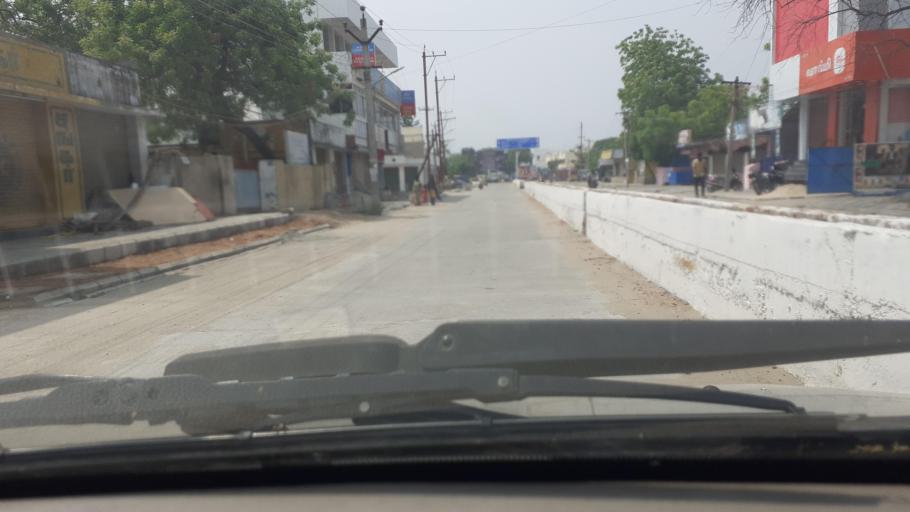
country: IN
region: Tamil Nadu
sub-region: Thoothukkudi
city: Korampallam
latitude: 8.8065
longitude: 78.1387
